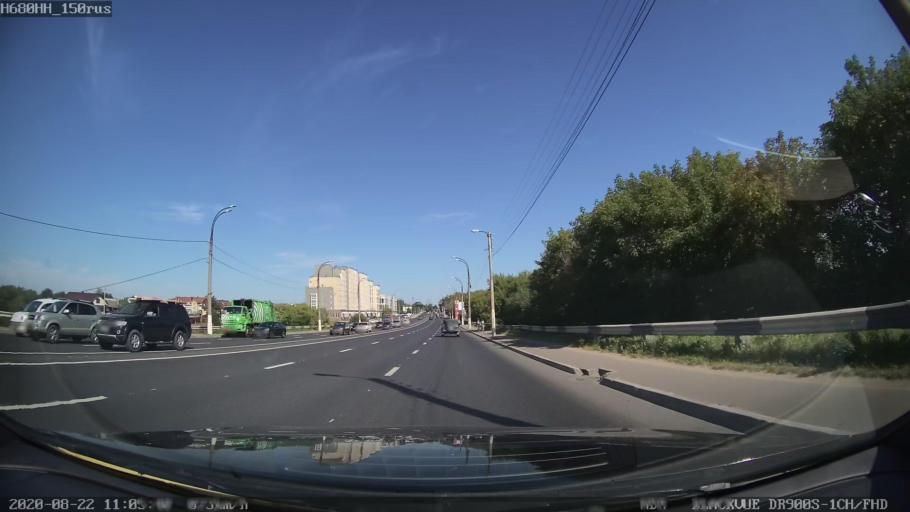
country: RU
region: Tverskaya
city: Tver
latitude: 56.8598
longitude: 35.9452
